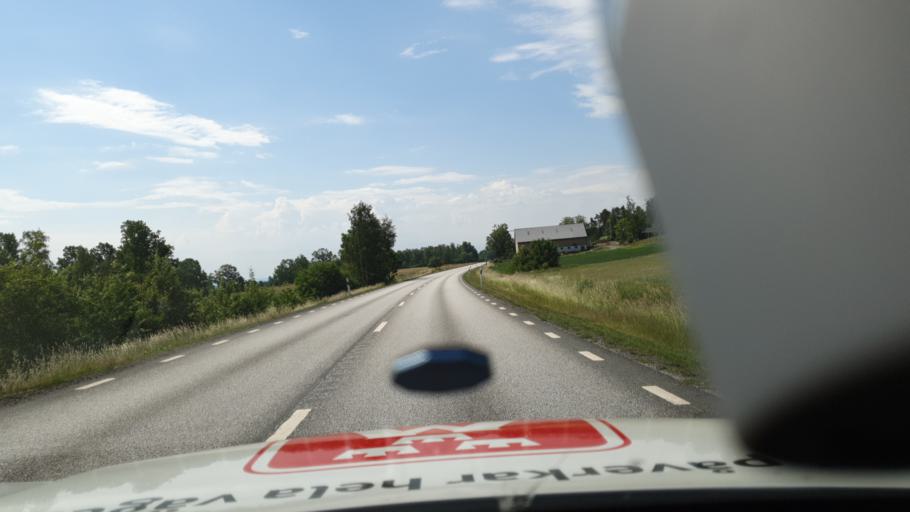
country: SE
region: Joenkoeping
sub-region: Habo Kommun
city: Habo
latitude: 58.0631
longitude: 14.1944
